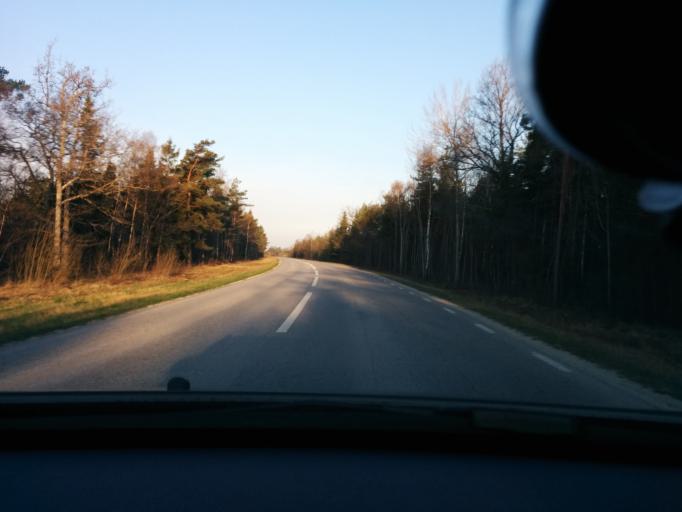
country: SE
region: Gotland
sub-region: Gotland
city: Visby
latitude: 57.6399
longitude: 18.4956
